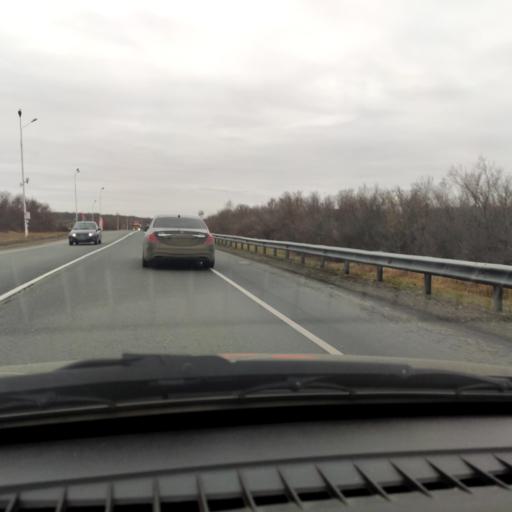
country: RU
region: Samara
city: Zhigulevsk
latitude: 53.3485
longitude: 49.4514
